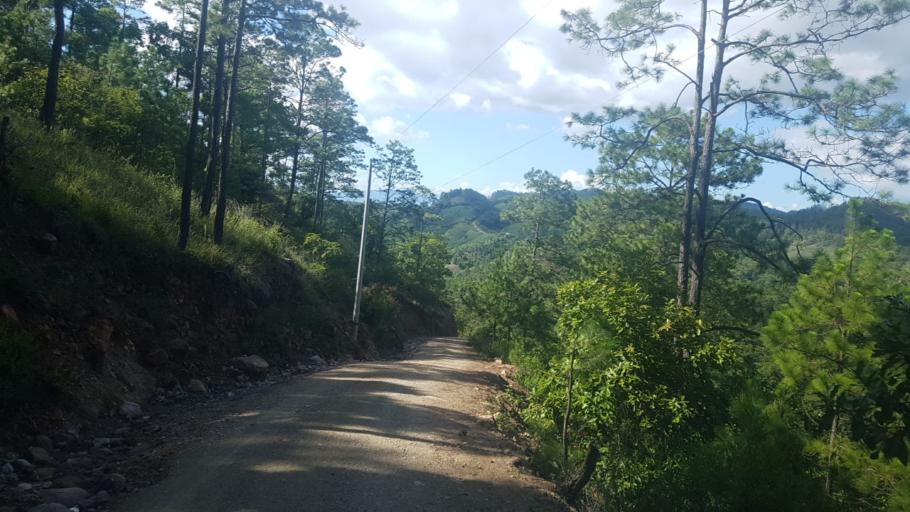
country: HN
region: Choluteca
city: Duyure
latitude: 13.6455
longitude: -86.6533
